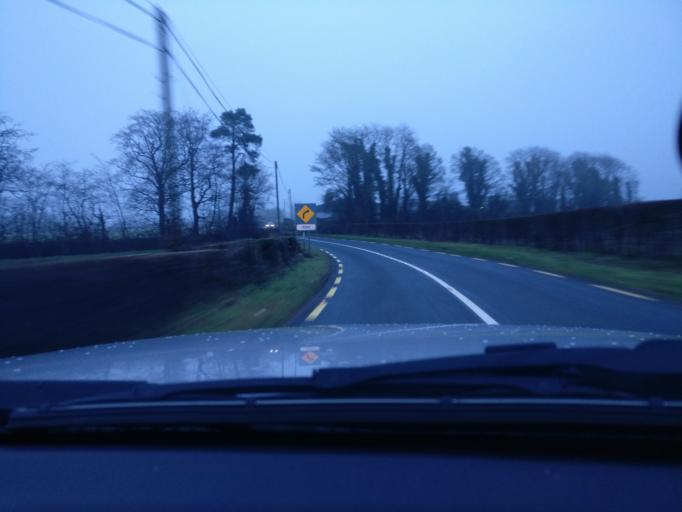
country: IE
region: Leinster
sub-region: An Mhi
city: Ballivor
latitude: 53.6108
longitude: -7.0424
